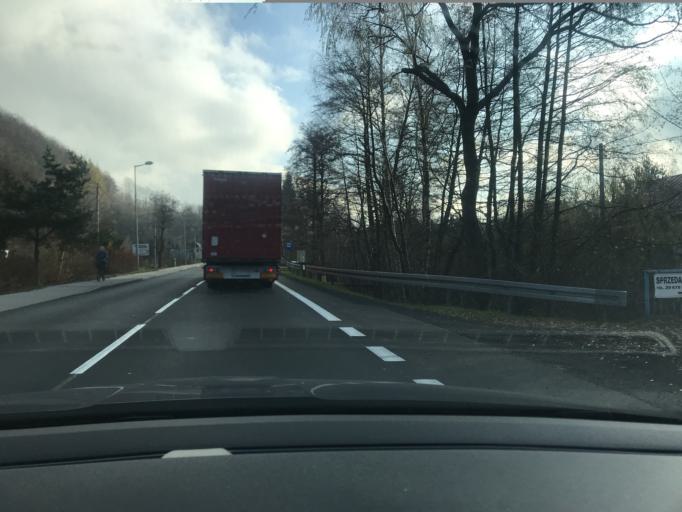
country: PL
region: Lower Silesian Voivodeship
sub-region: Powiat klodzki
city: Lewin Klodzki
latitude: 50.4117
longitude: 16.2695
